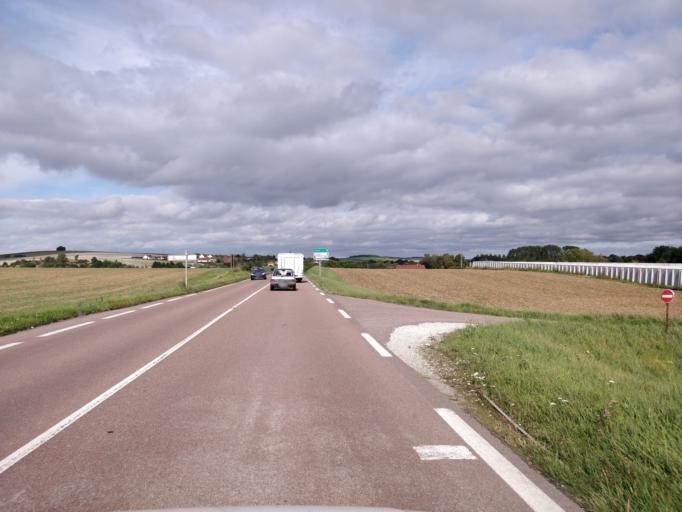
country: FR
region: Champagne-Ardenne
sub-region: Departement de l'Aube
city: Aix-en-Othe
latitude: 48.2491
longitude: 3.7156
